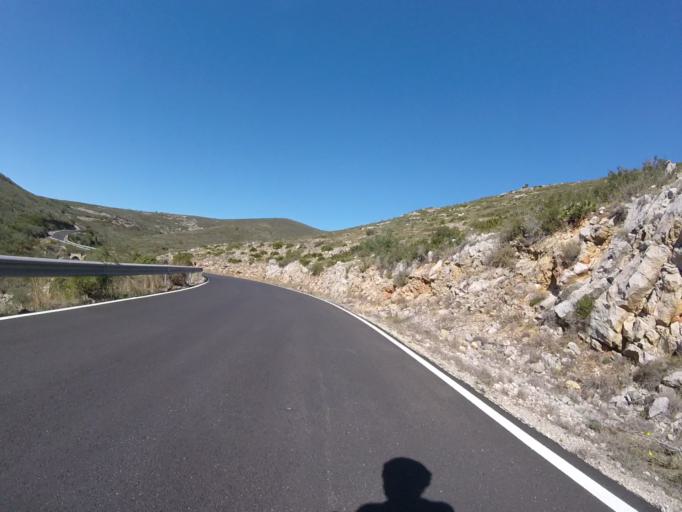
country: ES
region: Valencia
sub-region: Provincia de Castello
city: Cervera del Maestre
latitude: 40.4069
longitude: 0.2262
